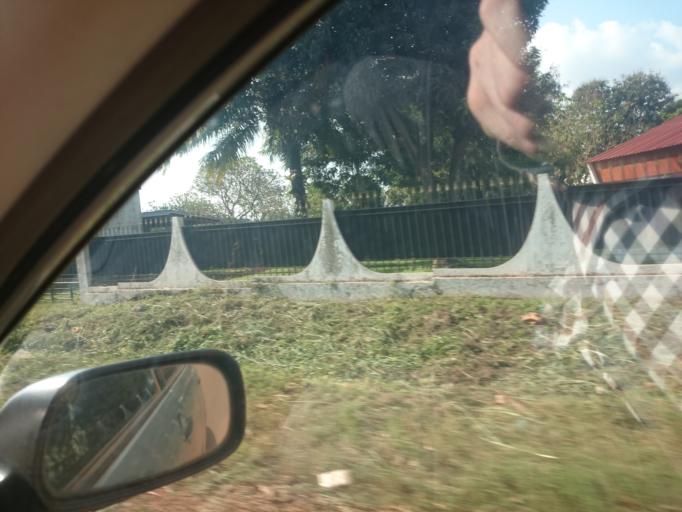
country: CF
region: Bangui
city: Bangui
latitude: 4.3797
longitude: 18.5628
